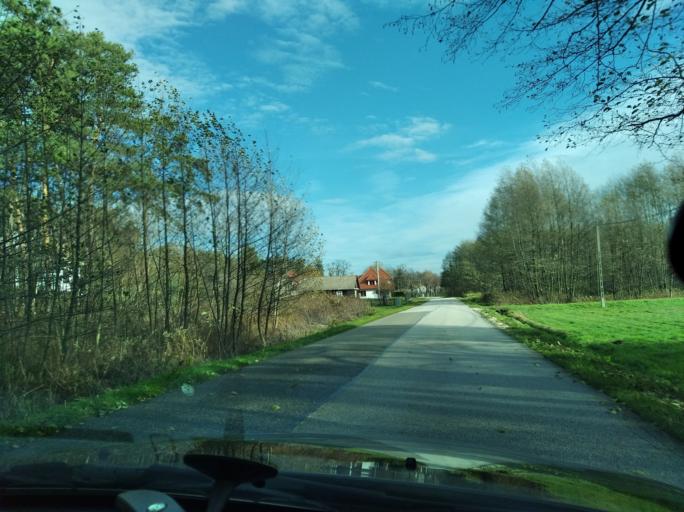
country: PL
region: Subcarpathian Voivodeship
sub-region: Powiat ropczycko-sedziszowski
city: Sedziszow Malopolski
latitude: 50.1158
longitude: 21.6935
